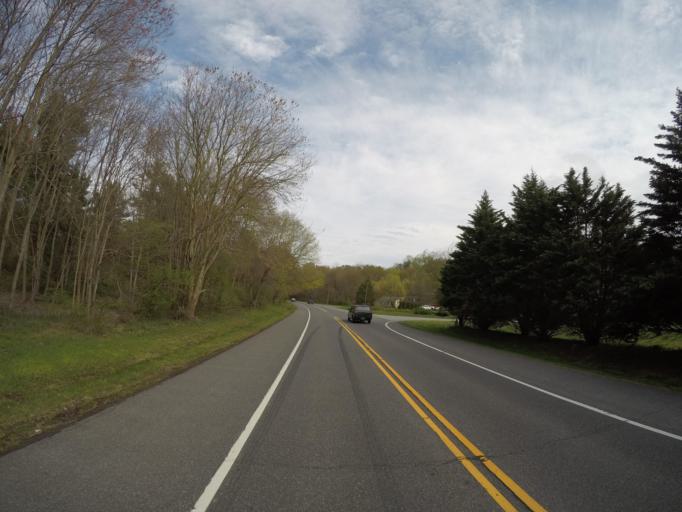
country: US
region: Delaware
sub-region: New Castle County
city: Glasgow
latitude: 39.5477
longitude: -75.7279
